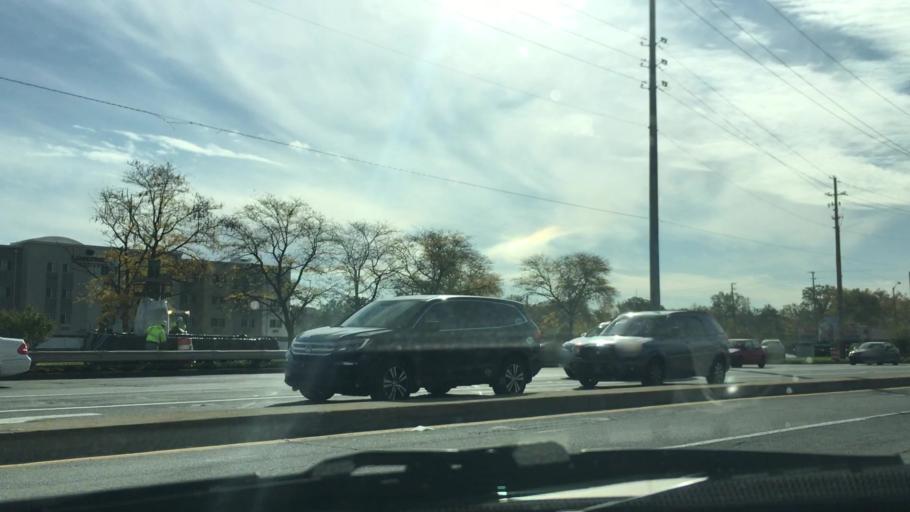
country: US
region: Indiana
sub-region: Marion County
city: Warren Park
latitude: 39.7979
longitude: -86.0456
